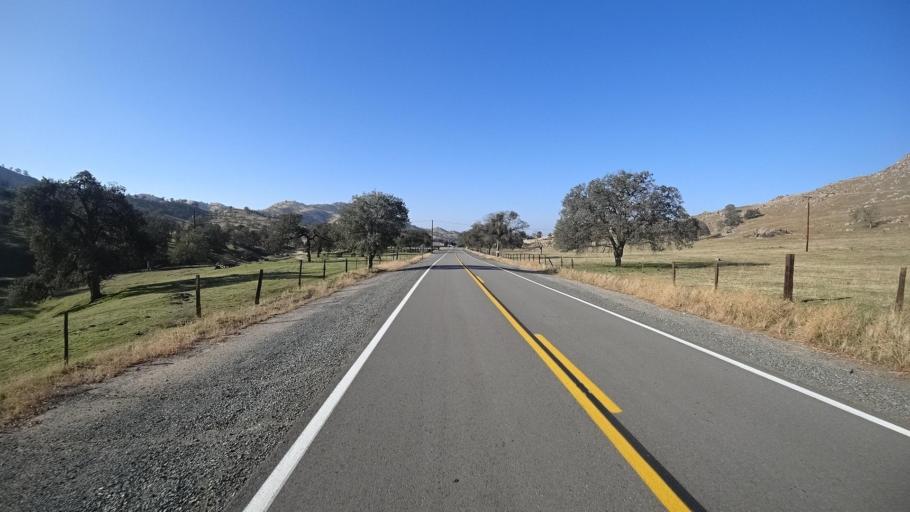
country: US
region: California
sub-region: Kern County
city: Alta Sierra
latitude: 35.7075
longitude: -118.8287
